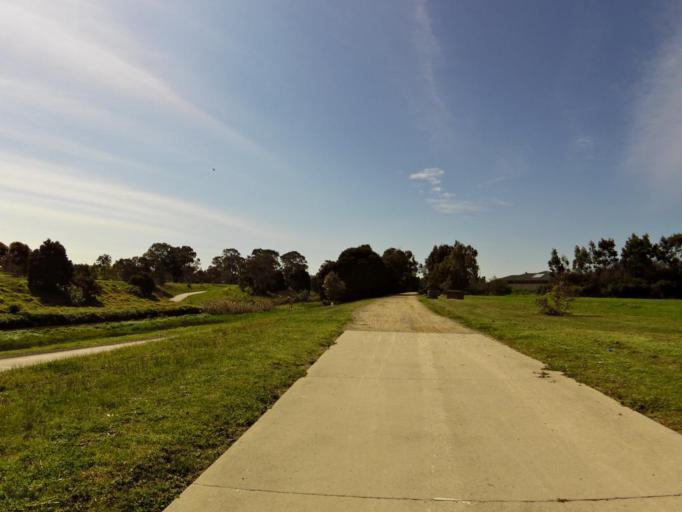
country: AU
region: Victoria
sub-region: Greater Dandenong
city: Dandenong
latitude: -38.0006
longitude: 145.1940
